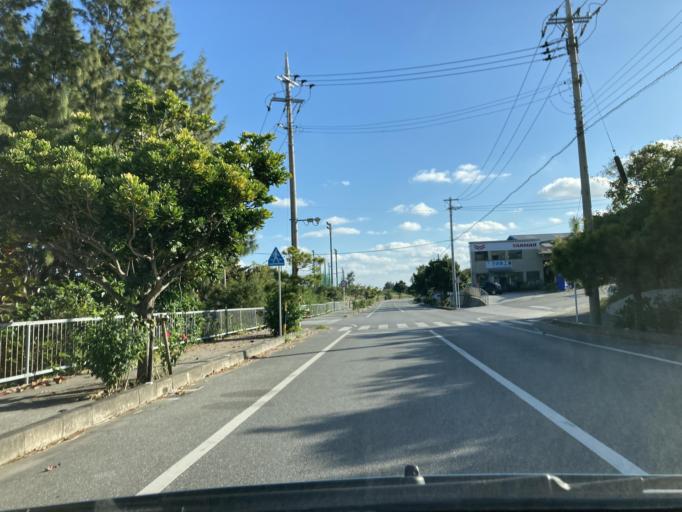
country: JP
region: Okinawa
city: Katsuren-haebaru
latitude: 26.3077
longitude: 127.9205
